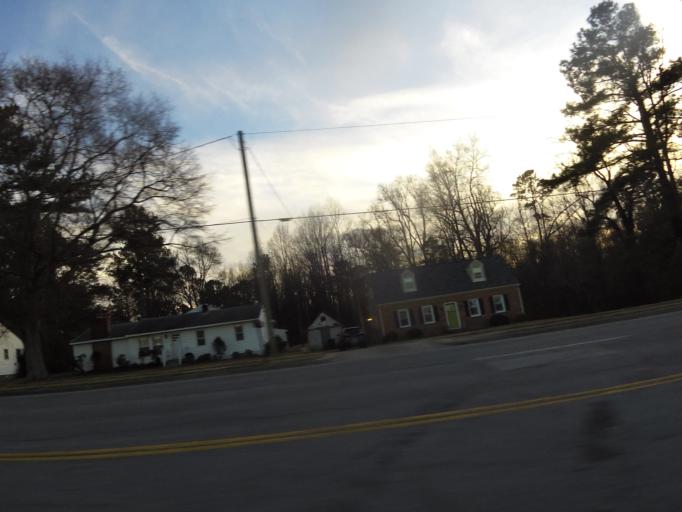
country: US
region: Virginia
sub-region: City of Franklin
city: Franklin
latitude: 36.6830
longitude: -76.9656
